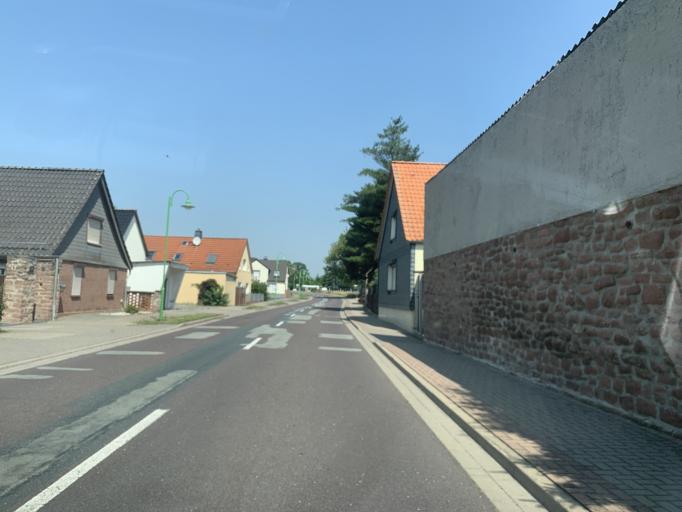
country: DE
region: Saxony-Anhalt
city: Erxleben
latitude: 52.2029
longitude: 11.2610
